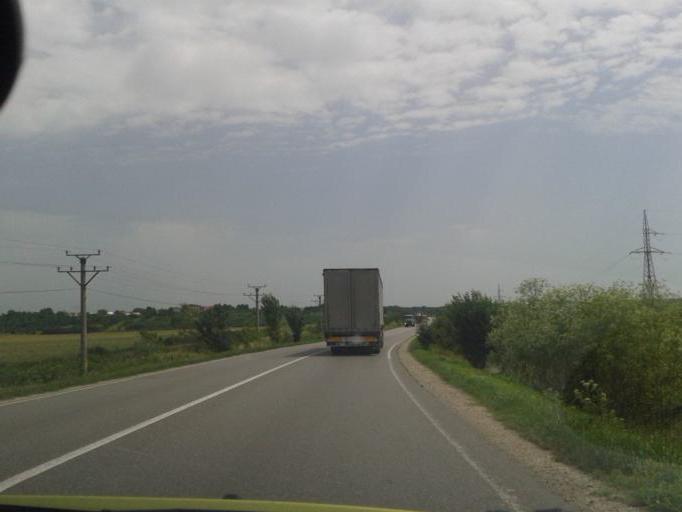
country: RO
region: Dambovita
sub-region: Comuna Dragodana
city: Dragodana
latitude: 44.7252
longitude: 25.3501
